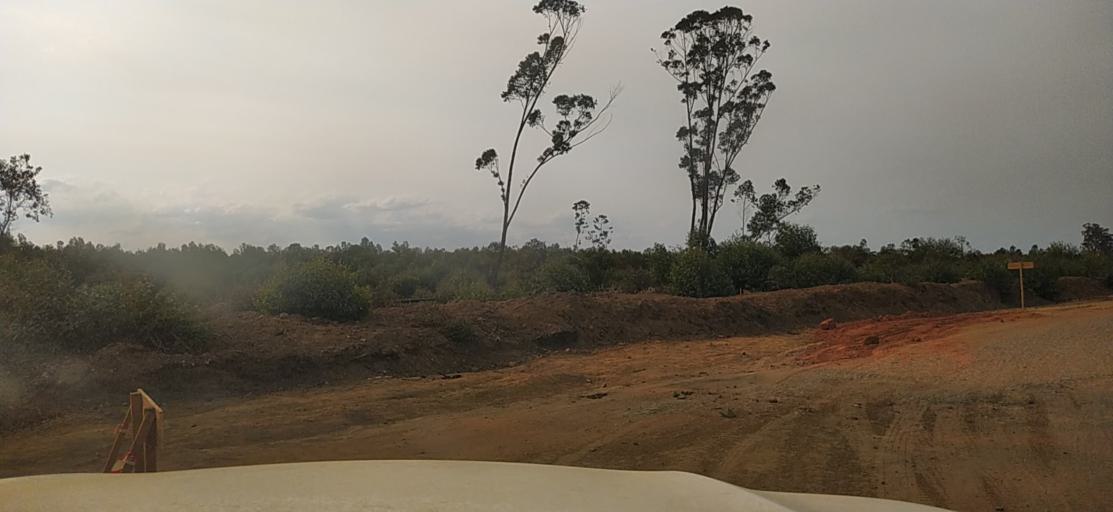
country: MG
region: Alaotra Mangoro
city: Moramanga
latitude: -18.6185
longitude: 48.2767
